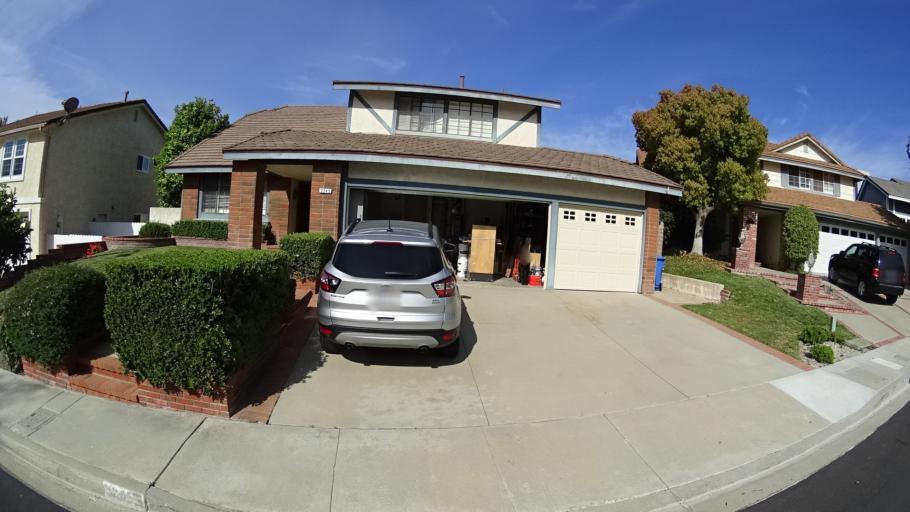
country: US
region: California
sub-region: Ventura County
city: Thousand Oaks
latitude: 34.2237
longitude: -118.8400
